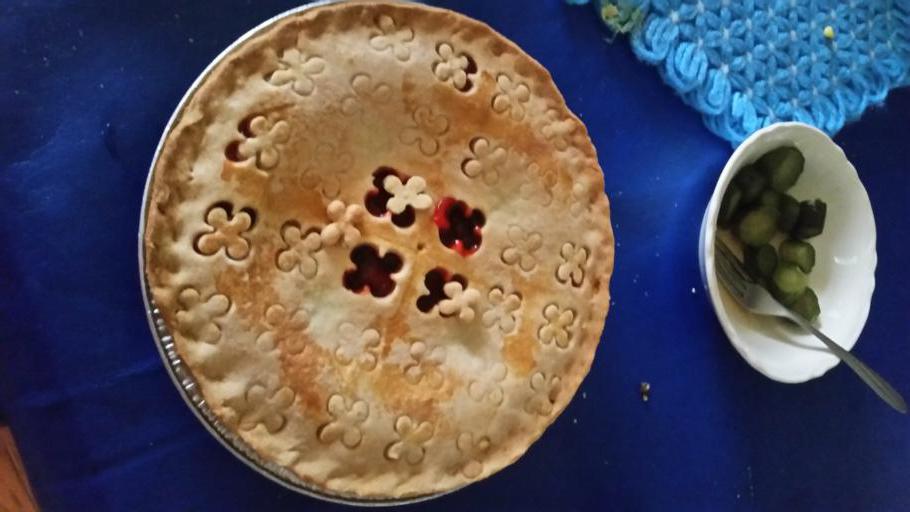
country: US
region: Wisconsin
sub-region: Clark County
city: Greenwood
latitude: 44.7033
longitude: -90.6078
